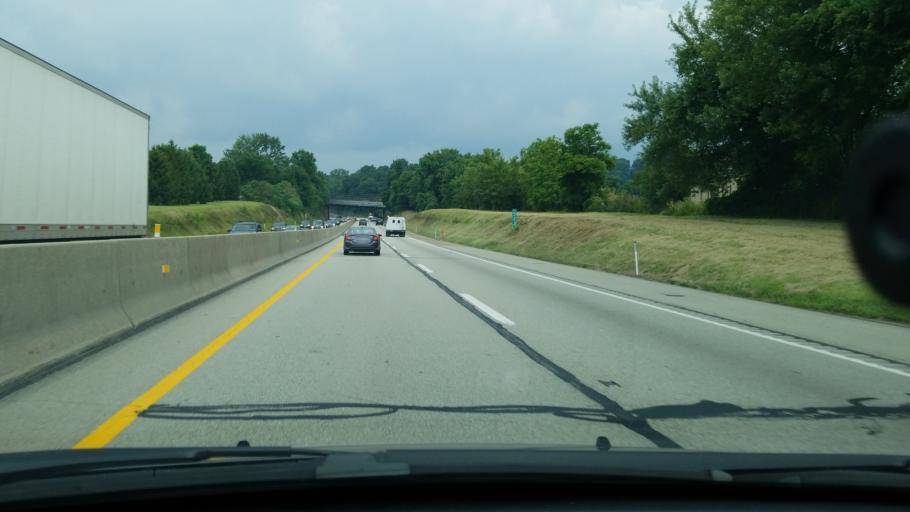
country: US
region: Pennsylvania
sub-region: Allegheny County
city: Plum
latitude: 40.4927
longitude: -79.7824
